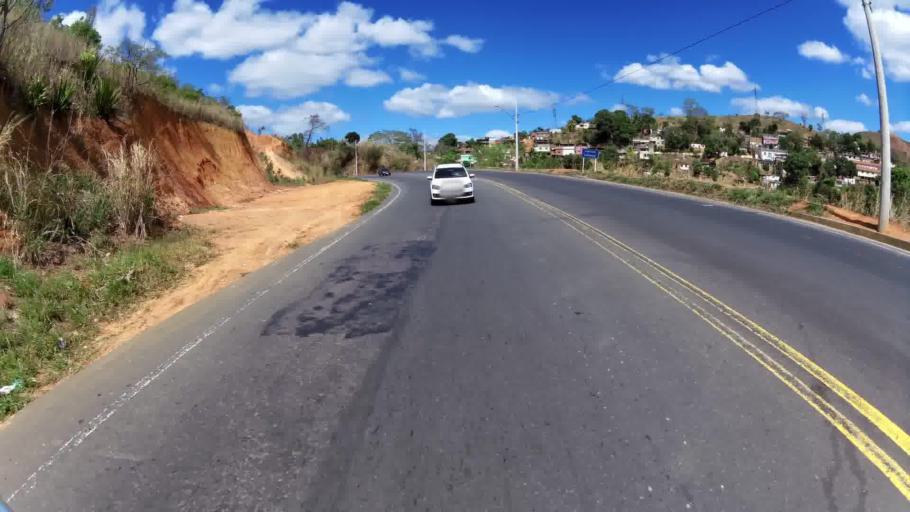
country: BR
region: Minas Gerais
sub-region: Alem Paraiba
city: Alem Paraiba
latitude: -21.8634
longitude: -42.6722
